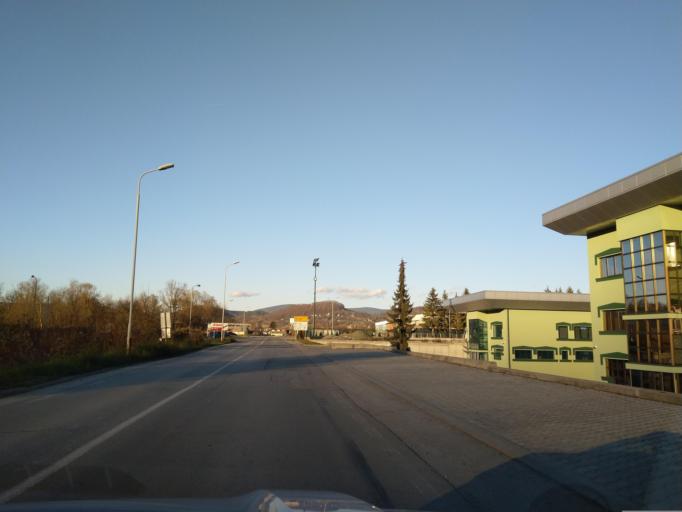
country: RS
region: Central Serbia
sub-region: Zlatiborski Okrug
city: Kosjeric
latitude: 43.9999
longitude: 19.9169
